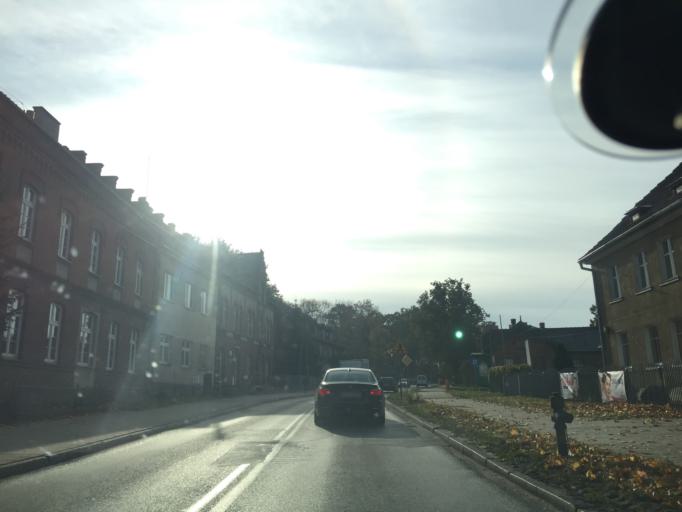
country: PL
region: Warmian-Masurian Voivodeship
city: Dobre Miasto
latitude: 53.9852
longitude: 20.4019
